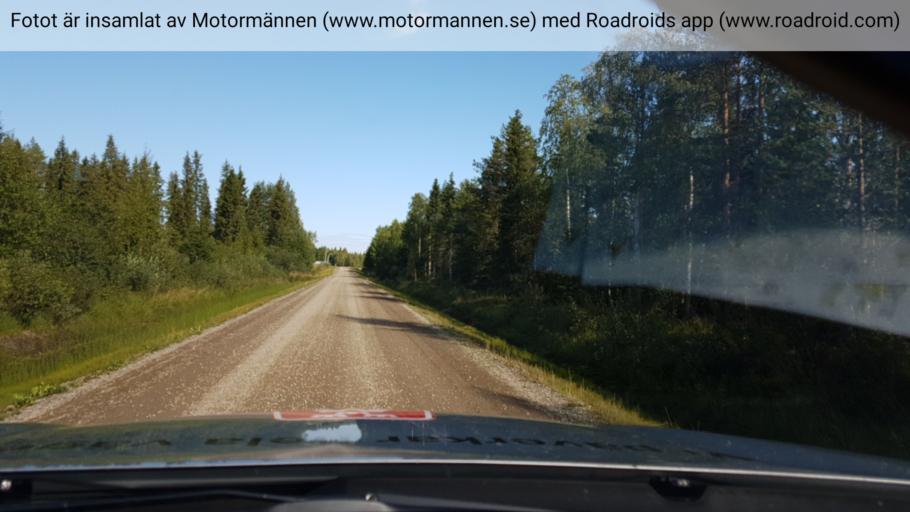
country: SE
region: Norrbotten
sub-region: Kalix Kommun
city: Kalix
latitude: 66.1882
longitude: 23.1982
